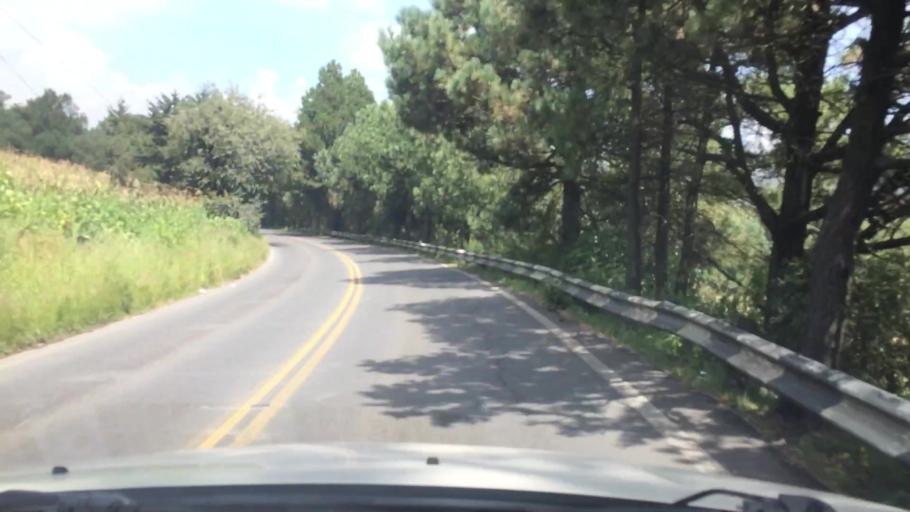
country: MX
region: Mexico City
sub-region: Tlalpan
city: Lomas de Tepemecatl
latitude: 19.2312
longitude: -99.2158
